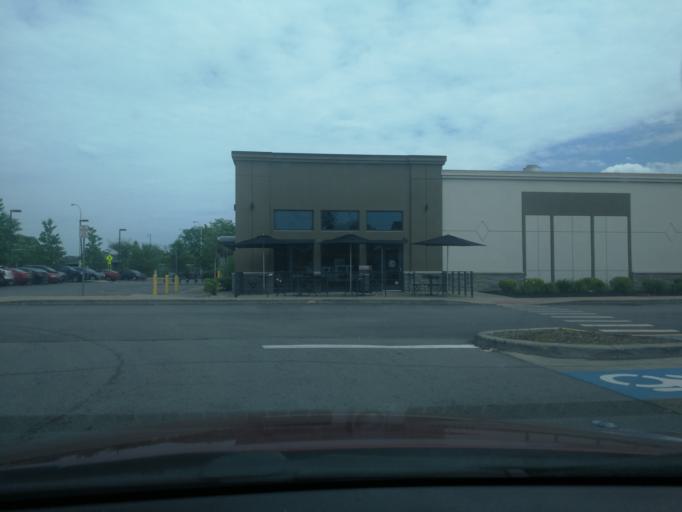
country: US
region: New York
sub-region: Monroe County
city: Greece
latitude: 43.2067
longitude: -77.6788
